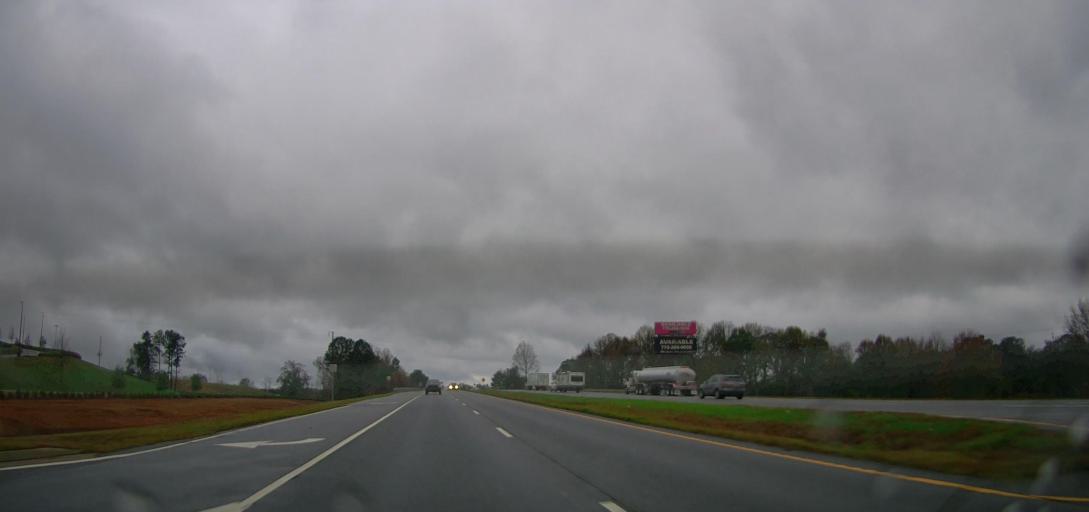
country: US
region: Georgia
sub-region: Jackson County
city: Commerce
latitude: 34.1861
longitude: -83.4359
